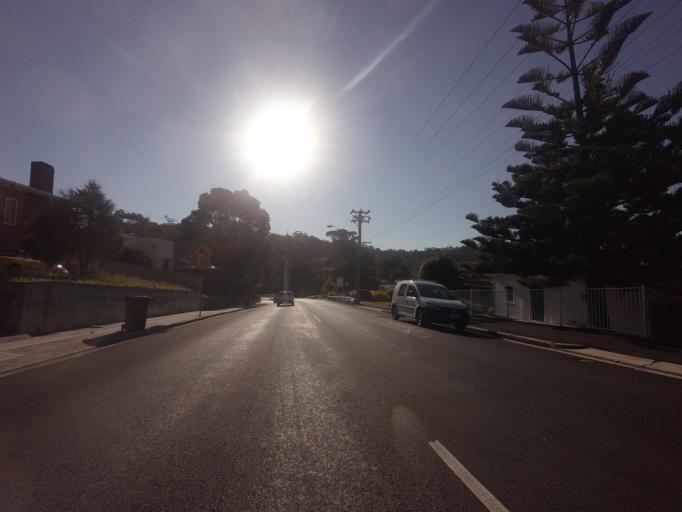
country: AU
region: Tasmania
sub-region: Glenorchy
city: West Moonah
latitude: -42.8619
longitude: 147.2866
